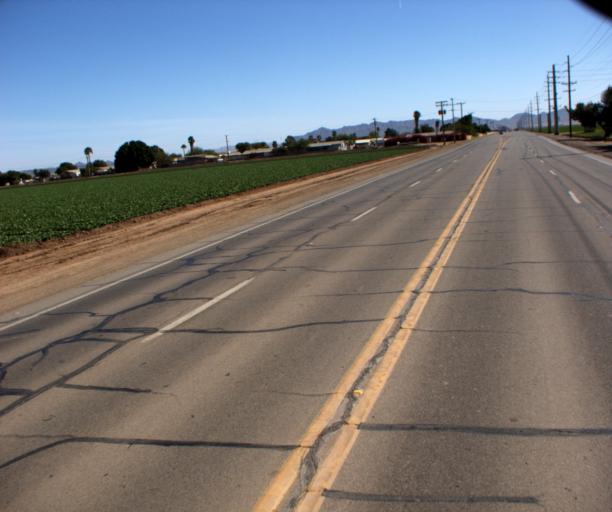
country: US
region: Arizona
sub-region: Yuma County
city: Yuma
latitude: 32.6991
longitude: -114.5323
